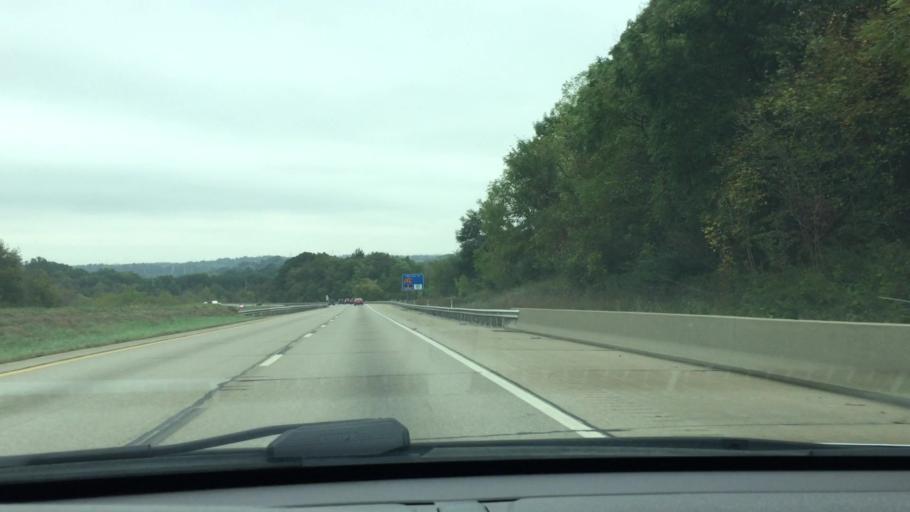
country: US
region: Pennsylvania
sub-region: Allegheny County
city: Bridgeville
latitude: 40.3431
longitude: -80.1236
